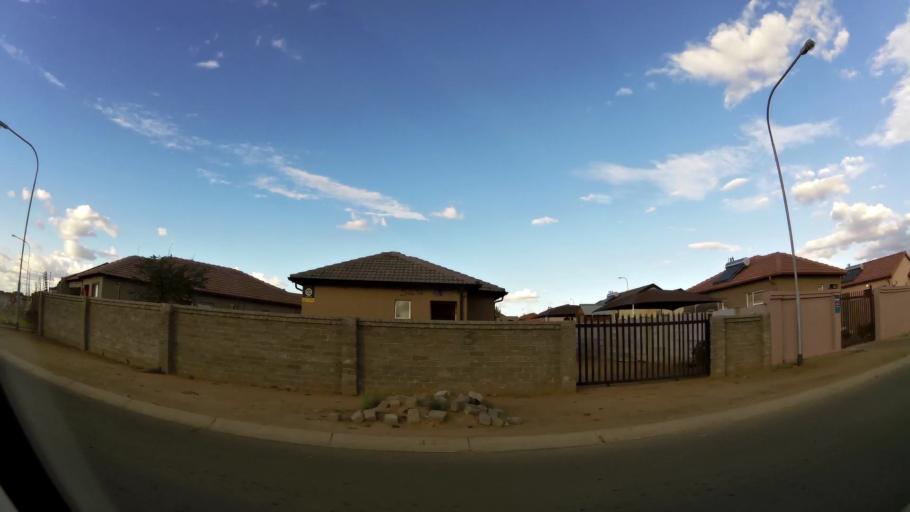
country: ZA
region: Limpopo
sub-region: Capricorn District Municipality
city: Polokwane
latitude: -23.9236
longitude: 29.4177
